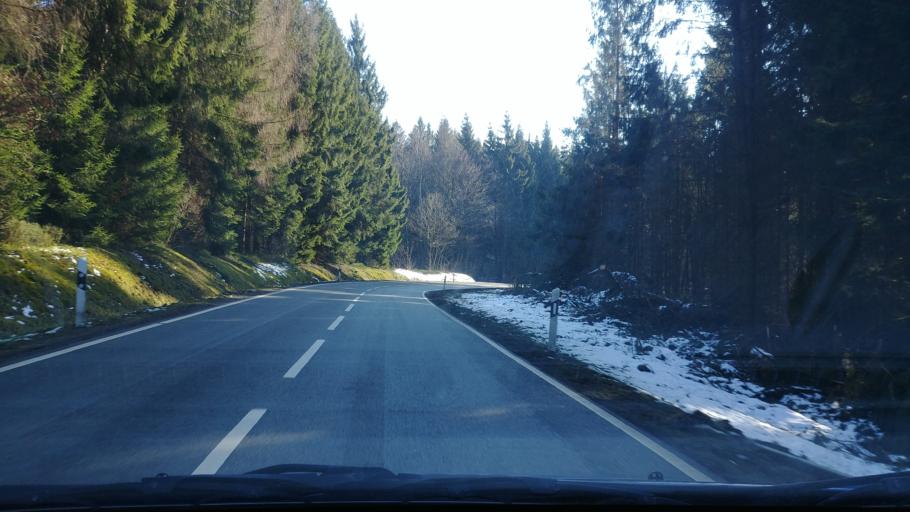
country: DE
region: Lower Saxony
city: Bodenfelde
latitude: 51.5968
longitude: 9.5236
